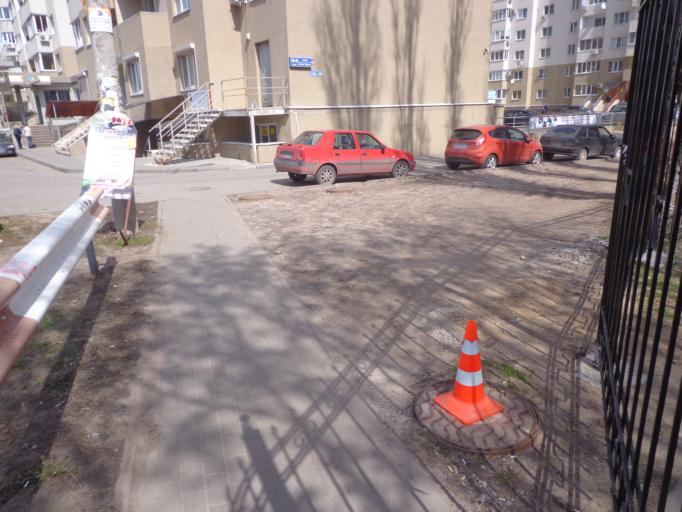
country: RU
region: Voronezj
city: Voronezh
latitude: 51.6740
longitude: 39.1945
